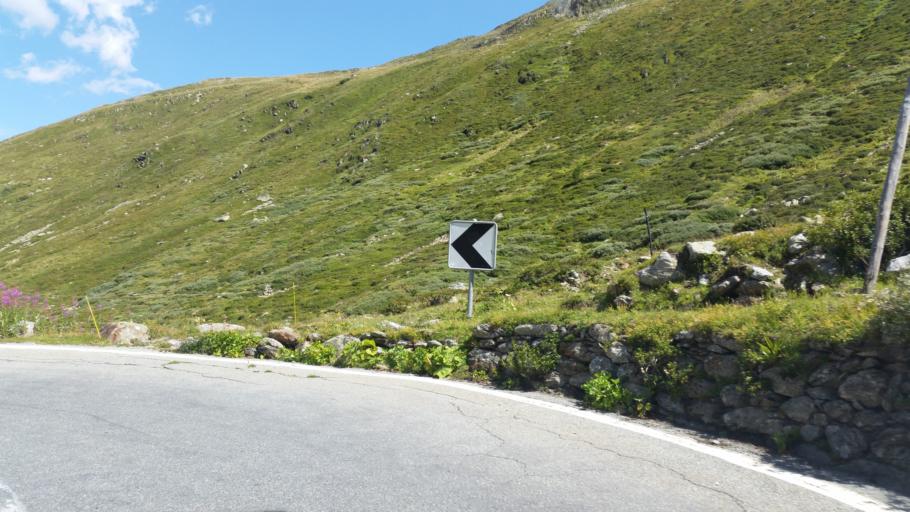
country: IT
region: Aosta Valley
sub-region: Valle d'Aosta
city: San Leonardo
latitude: 45.8861
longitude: 7.1881
